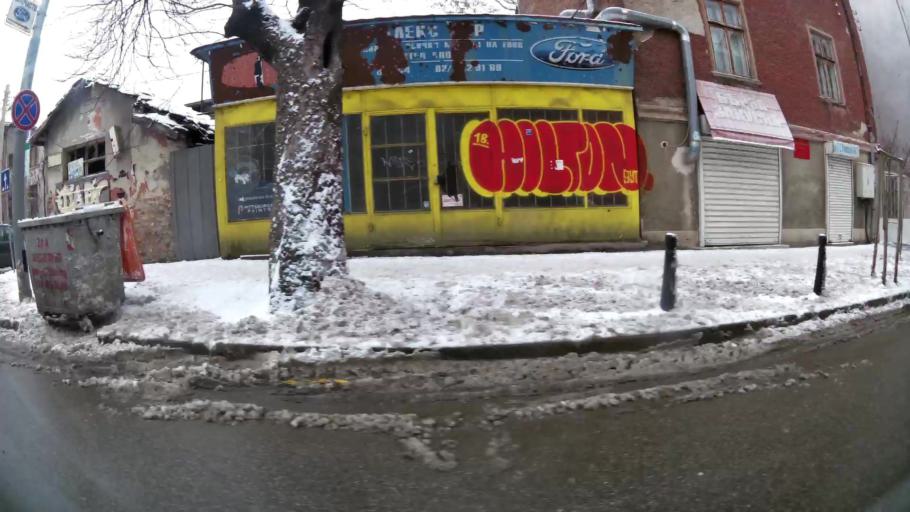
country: BG
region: Sofia-Capital
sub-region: Stolichna Obshtina
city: Sofia
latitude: 42.7069
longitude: 23.3283
